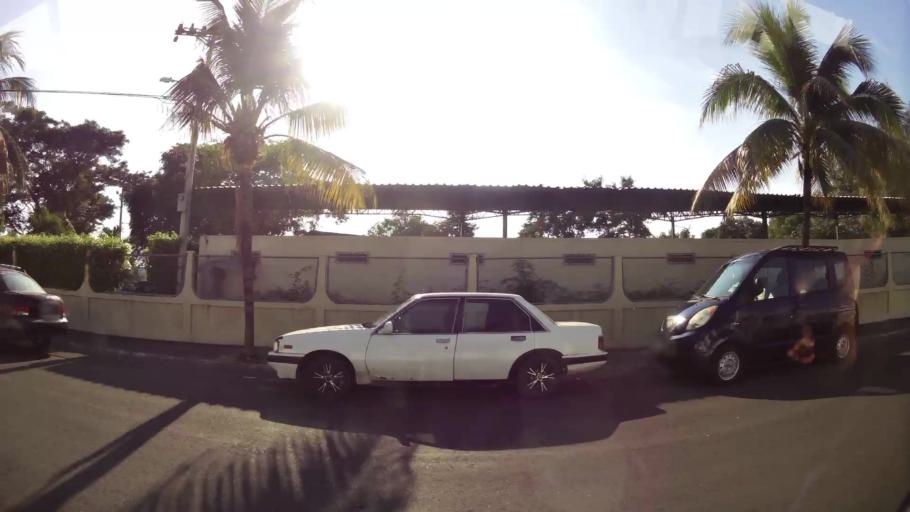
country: EC
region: Guayas
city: Santa Lucia
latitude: -2.1963
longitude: -79.9665
